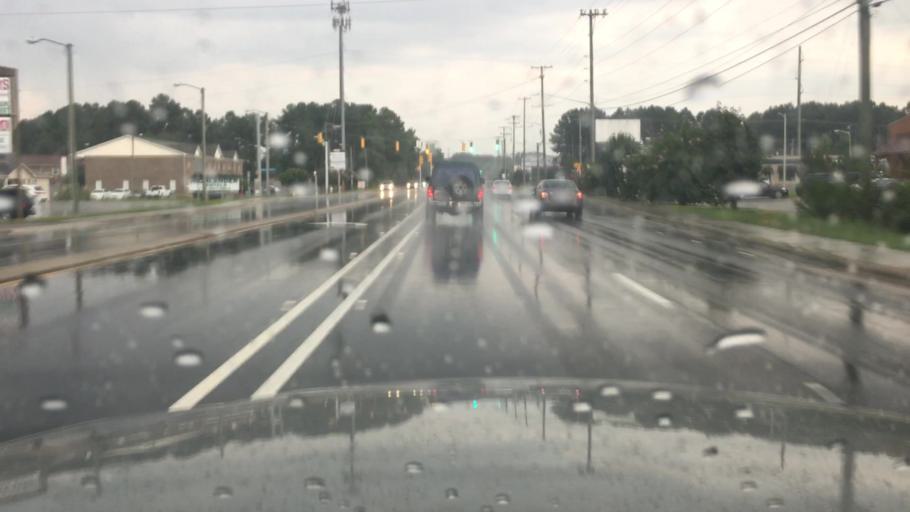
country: US
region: North Carolina
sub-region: Cumberland County
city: Fort Bragg
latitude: 35.0676
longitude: -79.0132
